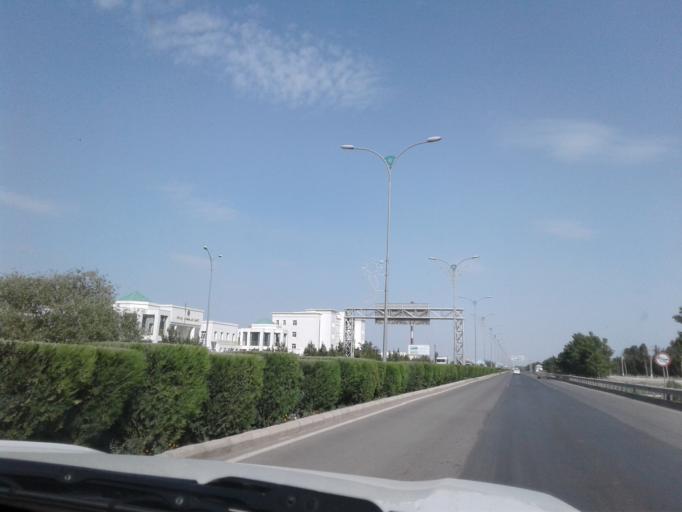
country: TM
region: Dasoguz
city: Dasoguz
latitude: 41.8357
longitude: 59.9290
